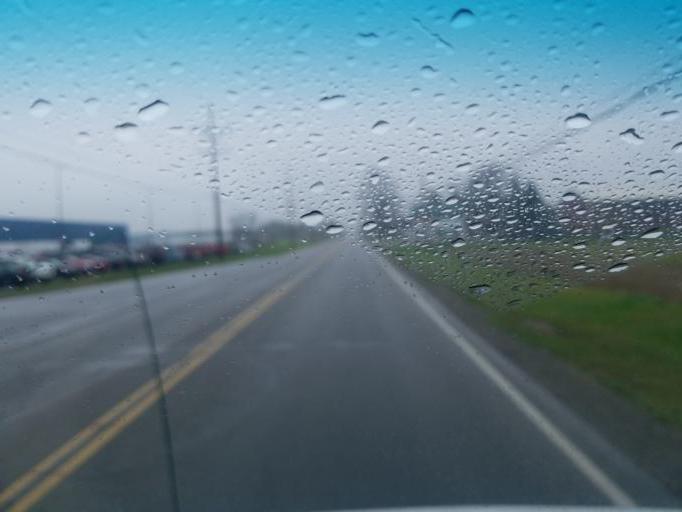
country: US
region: Ohio
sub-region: Hancock County
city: Findlay
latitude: 41.0990
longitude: -83.6499
